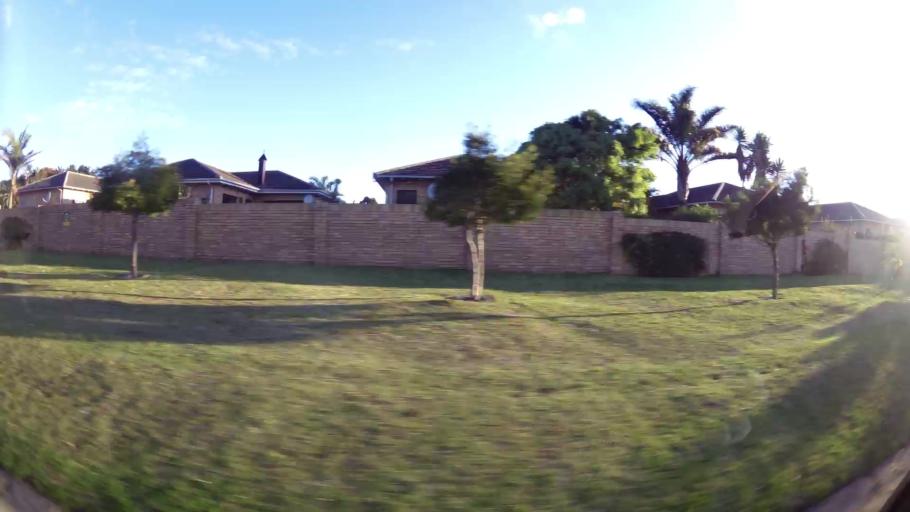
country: ZA
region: Eastern Cape
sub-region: Nelson Mandela Bay Metropolitan Municipality
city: Port Elizabeth
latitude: -33.9717
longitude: 25.4969
